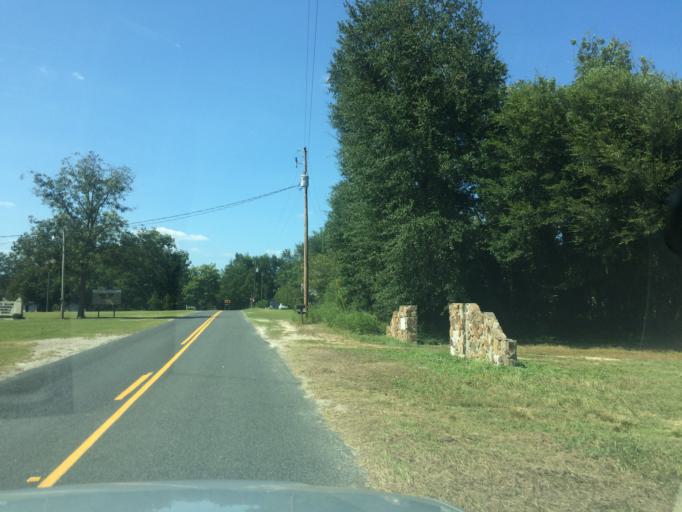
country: US
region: South Carolina
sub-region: Lexington County
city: Batesburg-Leesville
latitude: 33.6928
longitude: -81.4897
